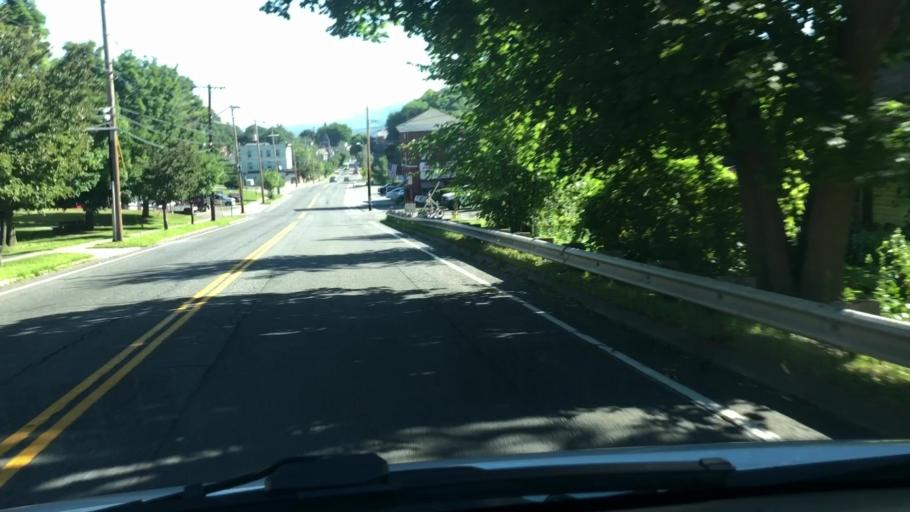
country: US
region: Massachusetts
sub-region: Berkshire County
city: Adams
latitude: 42.6135
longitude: -73.1244
